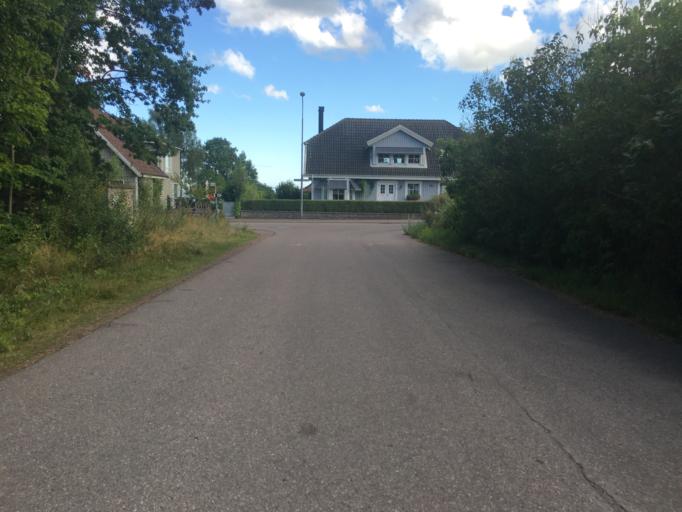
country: SE
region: Kalmar
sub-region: Kalmar Kommun
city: Kalmar
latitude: 56.7018
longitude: 16.3729
